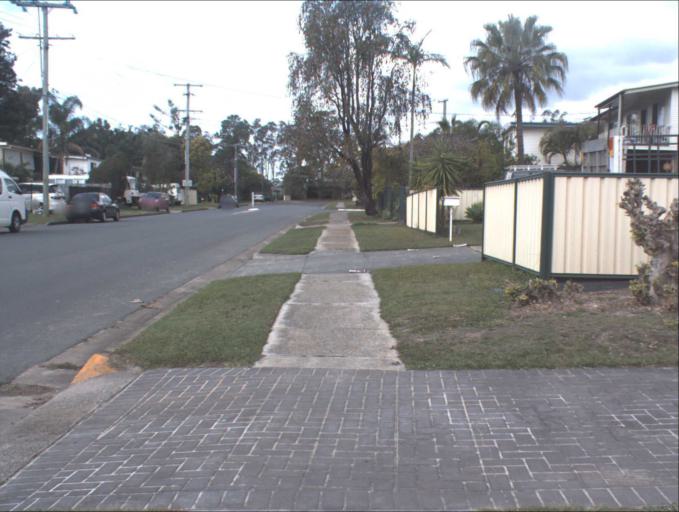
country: AU
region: Queensland
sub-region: Logan
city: Waterford West
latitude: -27.6825
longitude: 153.0964
